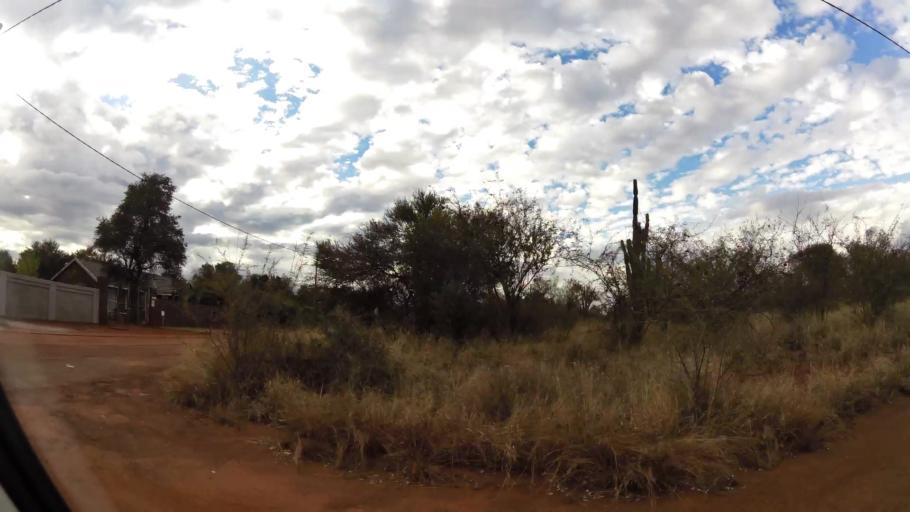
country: ZA
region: Limpopo
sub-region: Waterberg District Municipality
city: Modimolle
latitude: -24.5053
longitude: 28.7250
